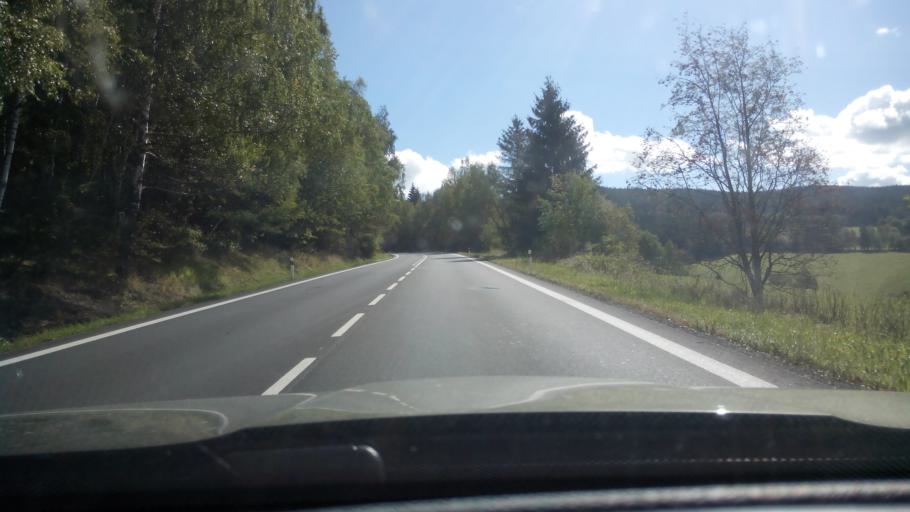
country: CZ
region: Jihocesky
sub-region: Okres Prachatice
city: Zdikov
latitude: 49.0787
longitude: 13.7028
